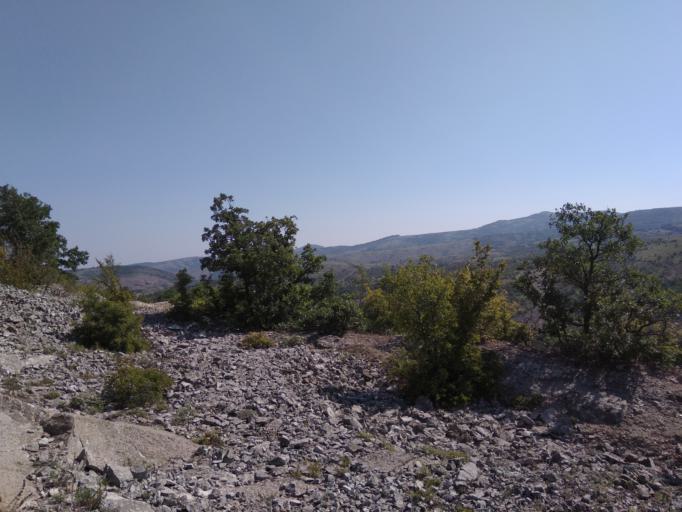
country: BG
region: Kurdzhali
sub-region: Obshtina Krumovgrad
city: Krumovgrad
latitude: 41.5146
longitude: 25.6647
